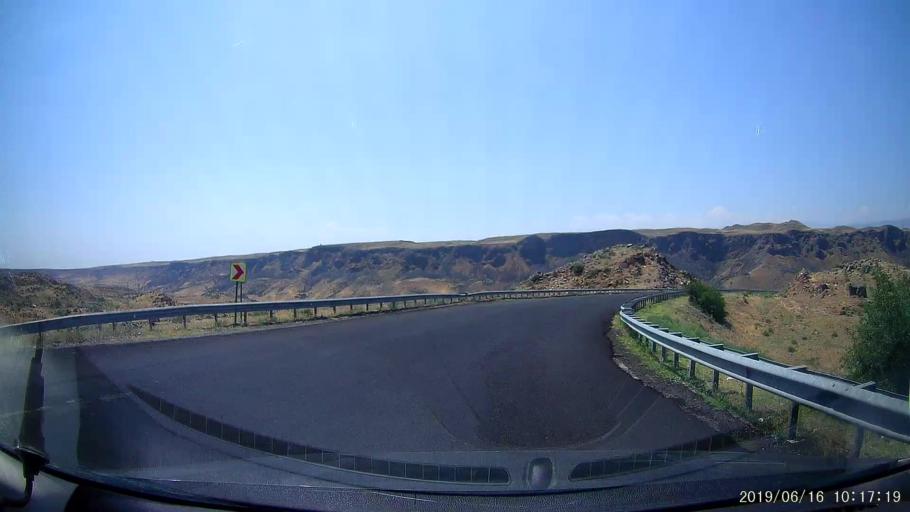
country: TR
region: Igdir
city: Tuzluca
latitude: 40.1690
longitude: 43.6821
